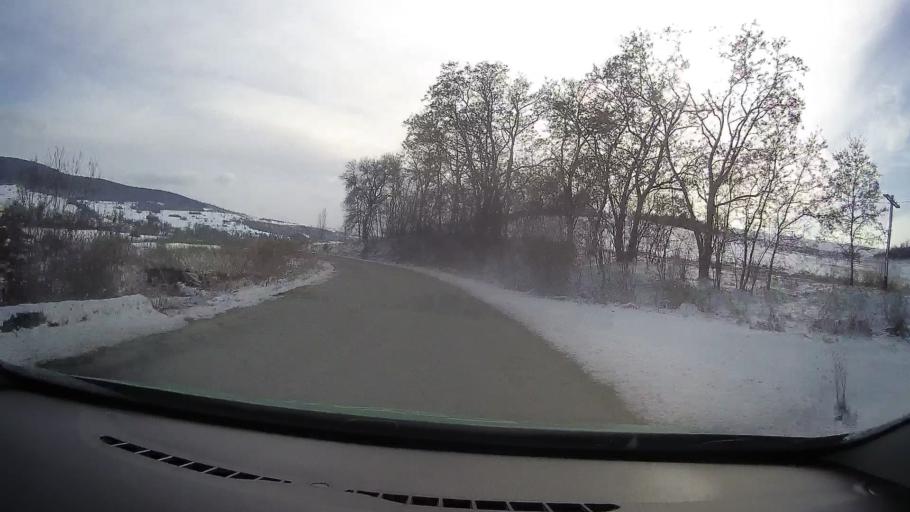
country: RO
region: Sibiu
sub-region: Comuna Iacobeni
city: Iacobeni
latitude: 46.0251
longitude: 24.7067
